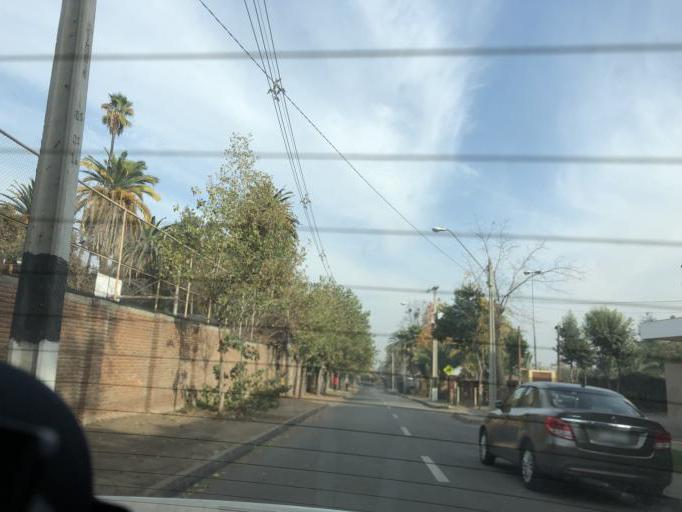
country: CL
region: Santiago Metropolitan
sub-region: Provincia de Cordillera
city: Puente Alto
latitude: -33.5643
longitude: -70.5533
